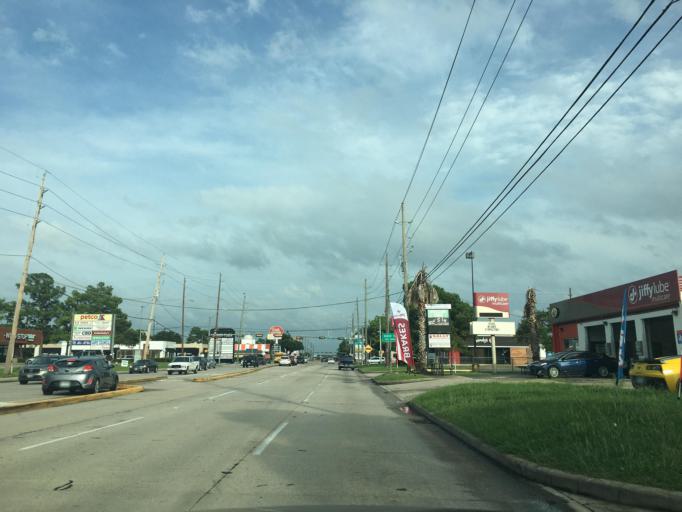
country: US
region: Texas
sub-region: Montgomery County
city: Oak Ridge North
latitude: 30.1266
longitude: -95.4509
